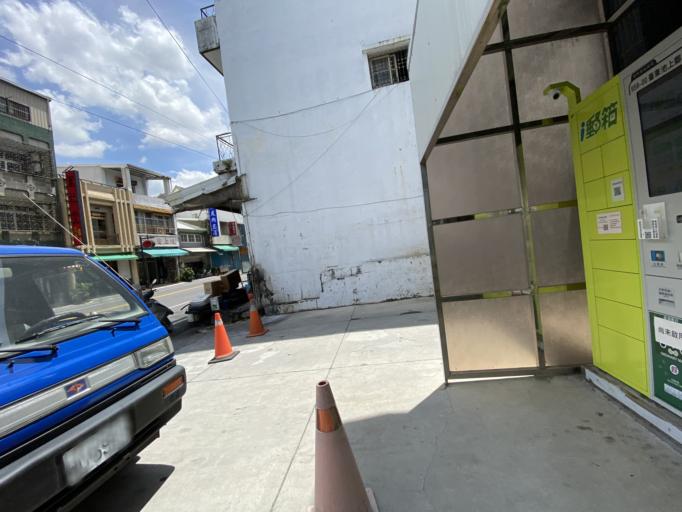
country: TW
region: Taiwan
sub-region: Taitung
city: Taitung
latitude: 23.1241
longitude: 121.2180
